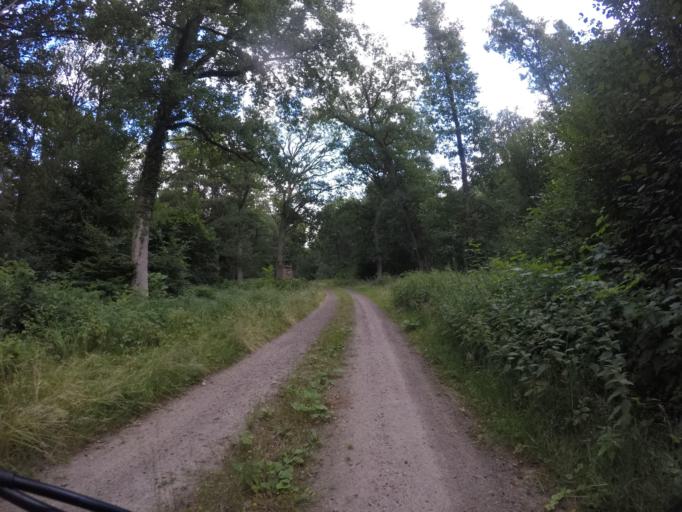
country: DE
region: Mecklenburg-Vorpommern
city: Lubtheen
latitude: 53.2795
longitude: 10.9840
